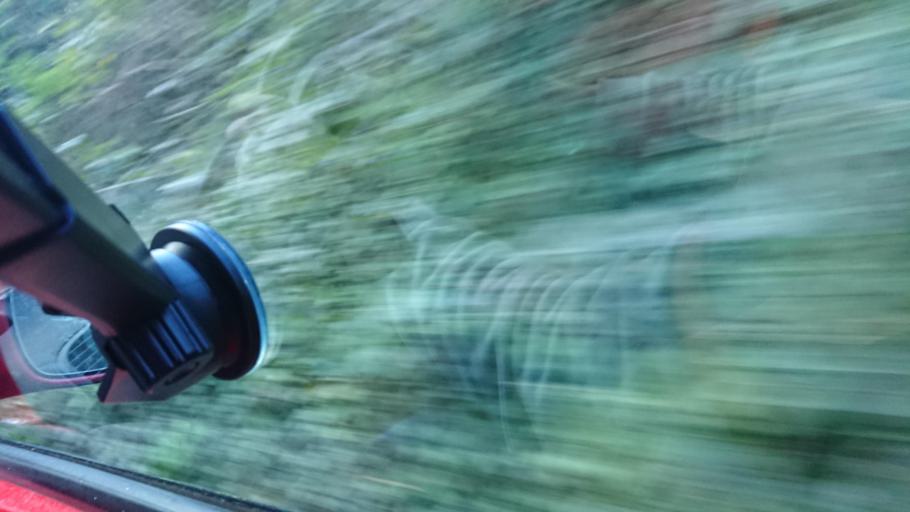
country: GB
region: England
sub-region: Cornwall
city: Looe
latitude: 50.3388
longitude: -4.4877
